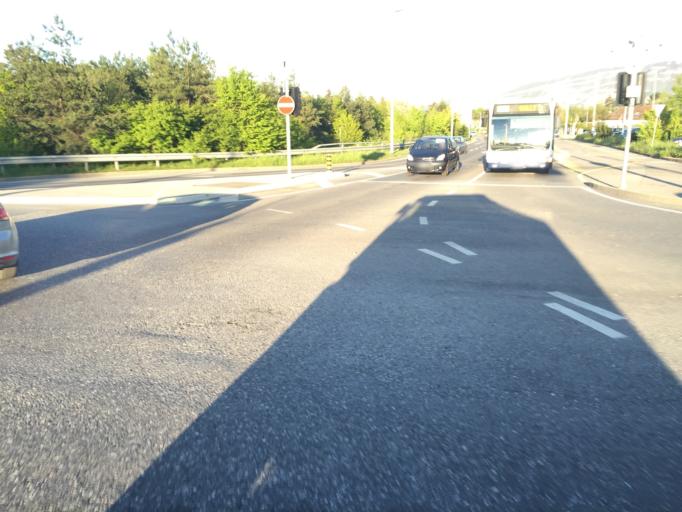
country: CH
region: Geneva
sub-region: Geneva
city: Confignon
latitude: 46.1790
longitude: 6.0841
